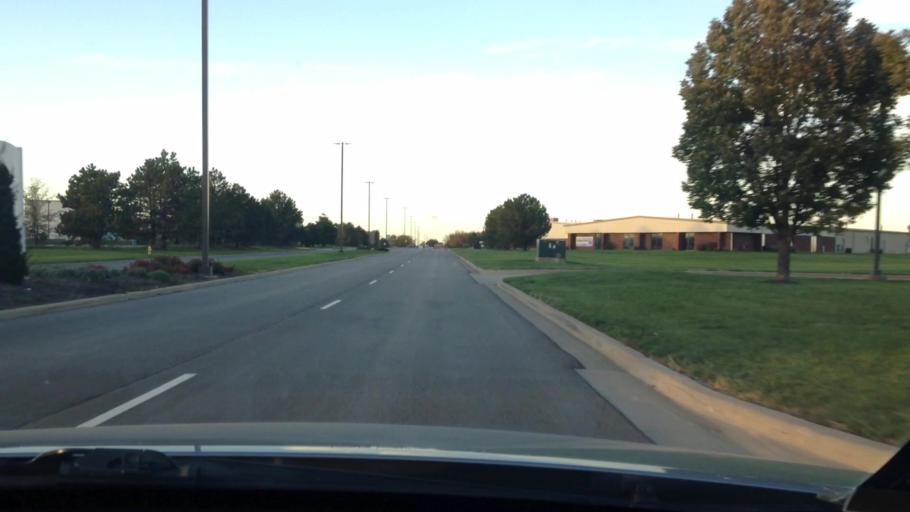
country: US
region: Kansas
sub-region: Johnson County
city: Gardner
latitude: 38.8235
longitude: -94.8992
